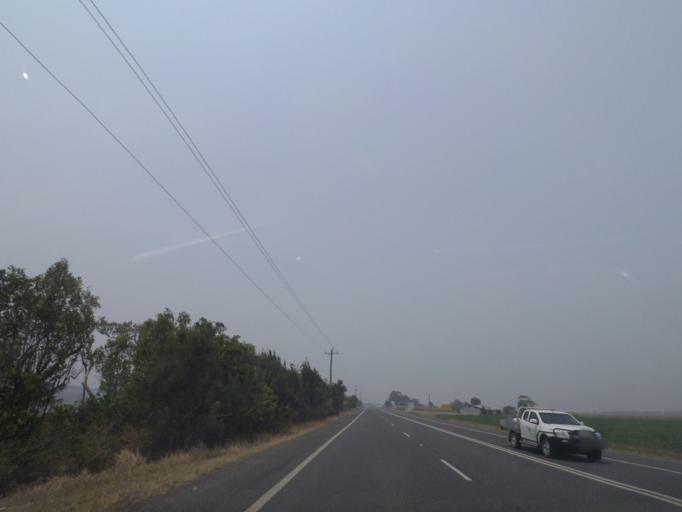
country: AU
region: New South Wales
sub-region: Richmond Valley
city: Evans Head
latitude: -28.9975
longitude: 153.4503
